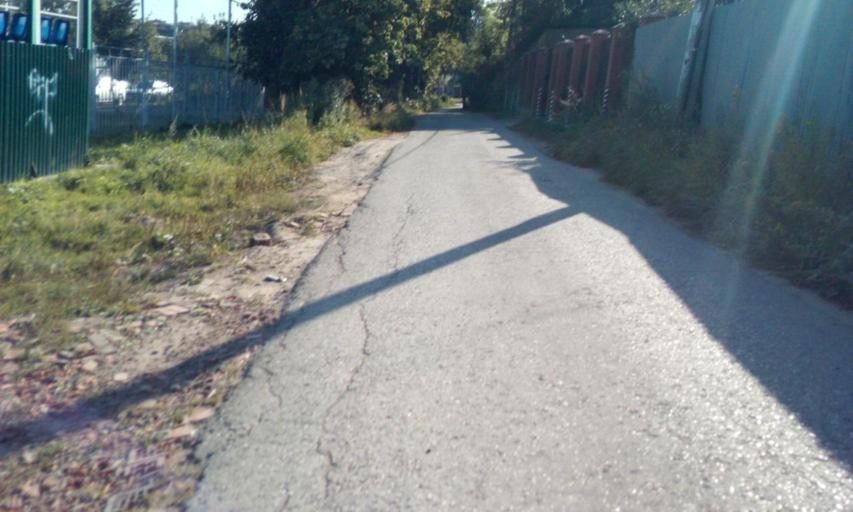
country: RU
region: Moskovskaya
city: Lesnoy Gorodok
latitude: 55.6649
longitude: 37.2392
